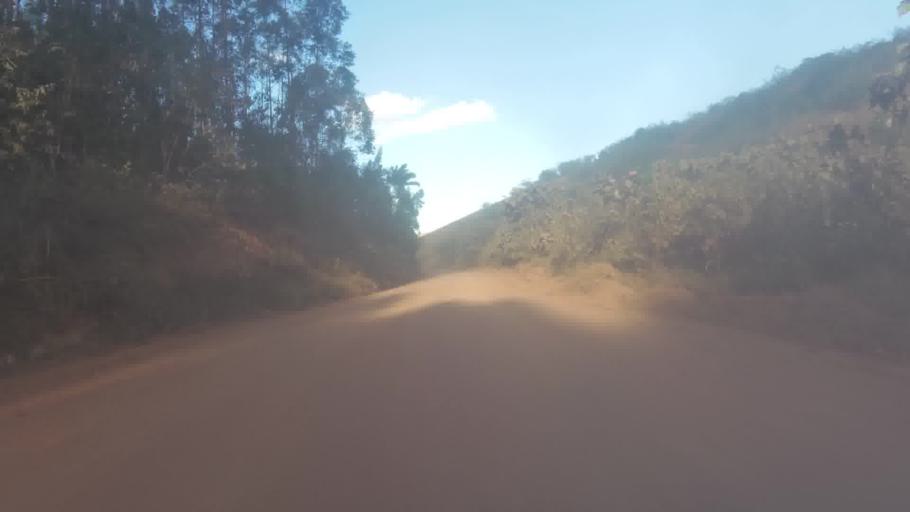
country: BR
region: Espirito Santo
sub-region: Mimoso Do Sul
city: Mimoso do Sul
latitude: -21.1023
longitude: -41.1353
